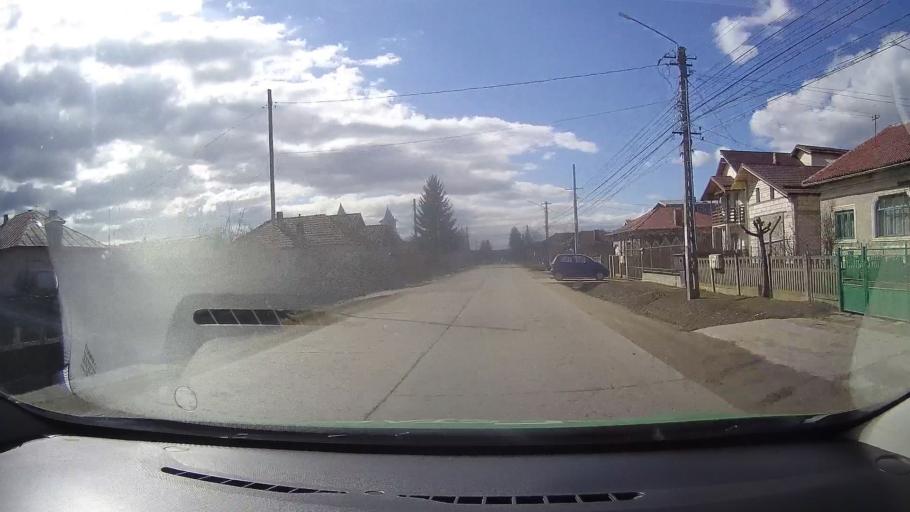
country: RO
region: Dambovita
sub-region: Comuna Branesti
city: Branesti
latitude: 45.0342
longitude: 25.4141
